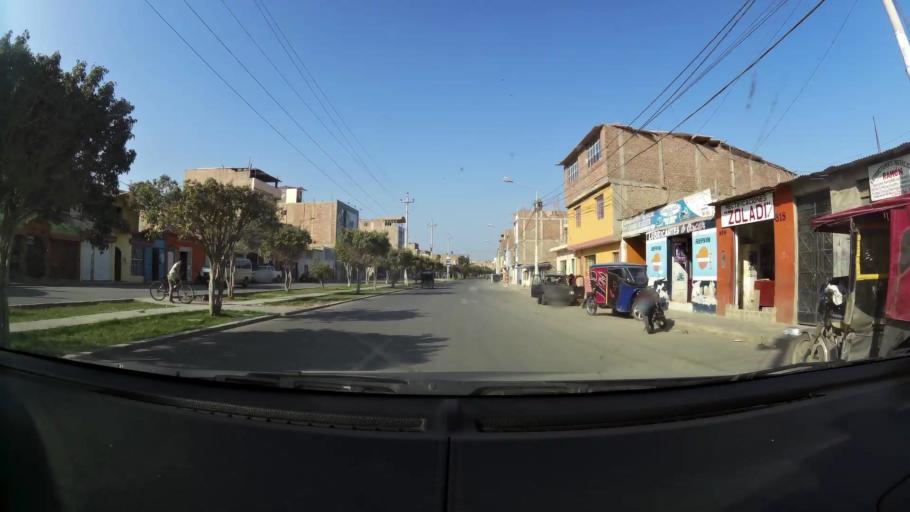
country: PE
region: Lambayeque
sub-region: Provincia de Chiclayo
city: Chiclayo
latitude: -6.7638
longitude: -79.8498
